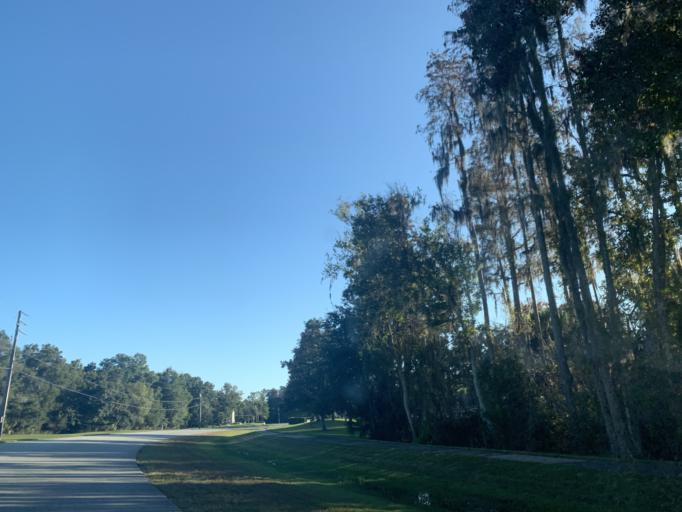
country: US
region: Florida
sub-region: Pinellas County
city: East Lake
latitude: 28.1241
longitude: -82.6917
